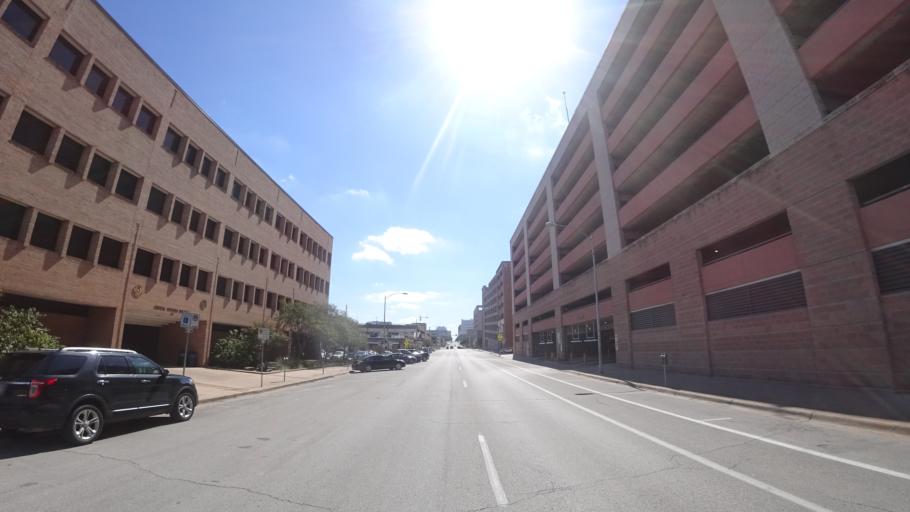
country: US
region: Texas
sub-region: Travis County
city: Austin
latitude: 30.2788
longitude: -97.7362
